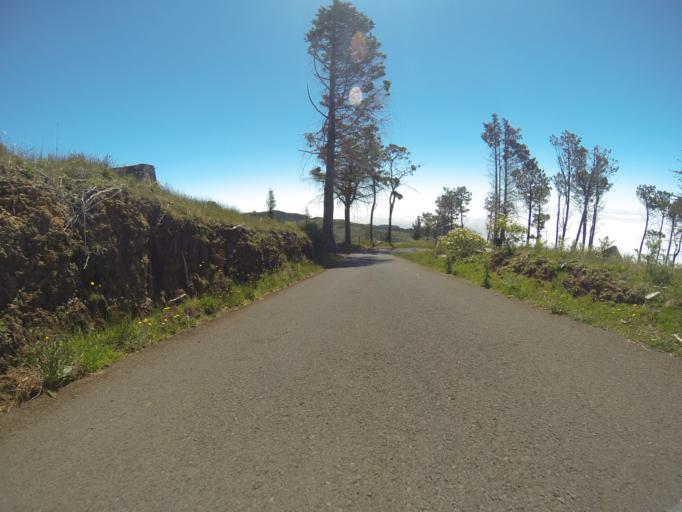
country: PT
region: Madeira
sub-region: Funchal
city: Nossa Senhora do Monte
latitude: 32.7084
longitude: -16.9102
